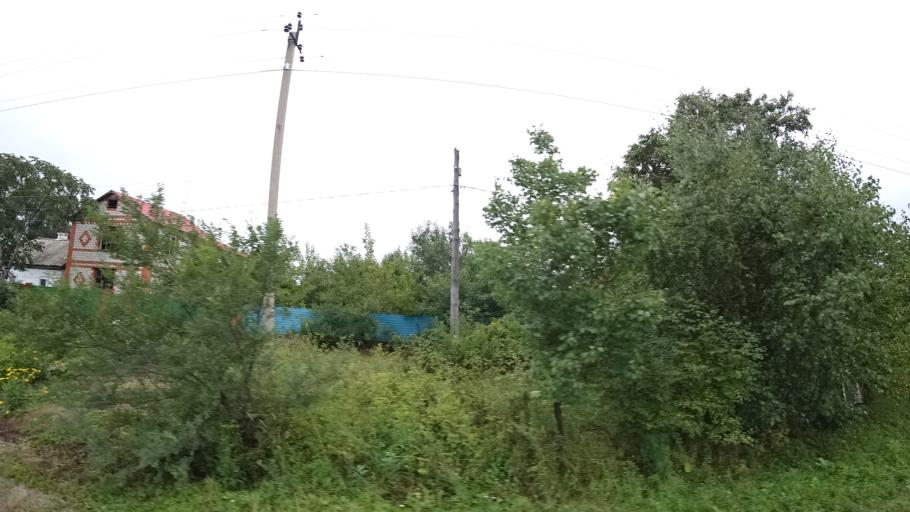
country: RU
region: Primorskiy
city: Chernigovka
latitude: 44.3350
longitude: 132.5963
